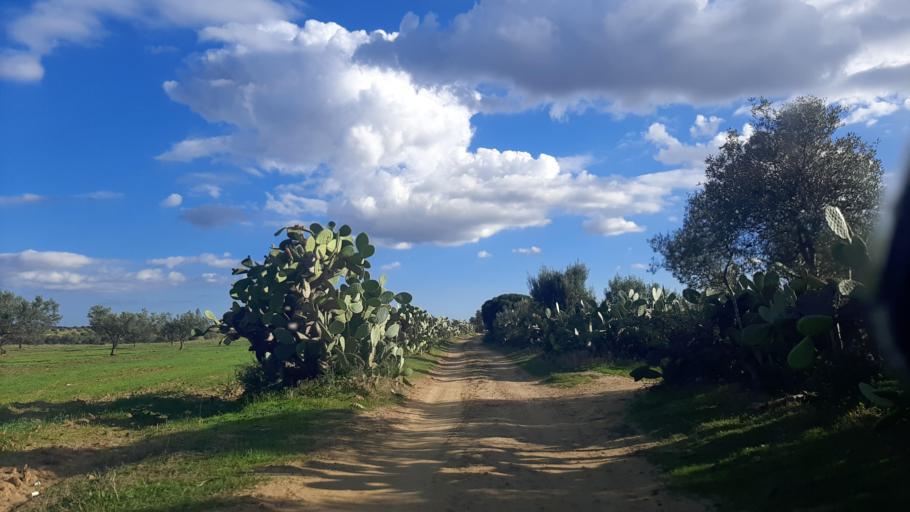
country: TN
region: Nabul
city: Bu `Urqub
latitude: 36.4637
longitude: 10.4843
